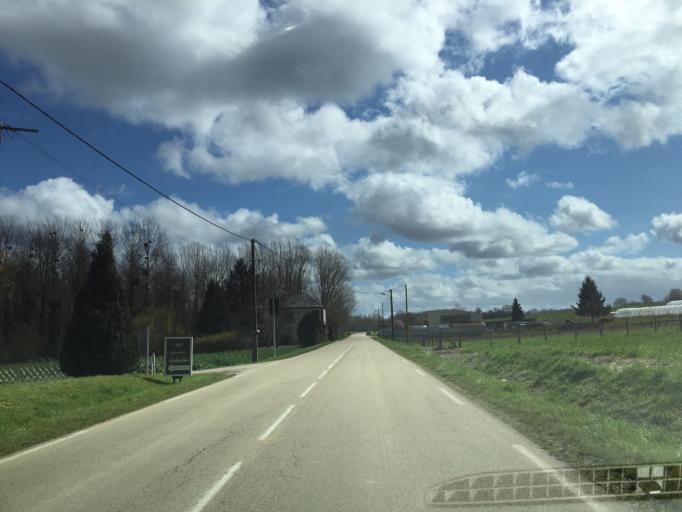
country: FR
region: Bourgogne
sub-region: Departement de l'Yonne
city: Aillant-sur-Tholon
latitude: 47.8426
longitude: 3.3955
